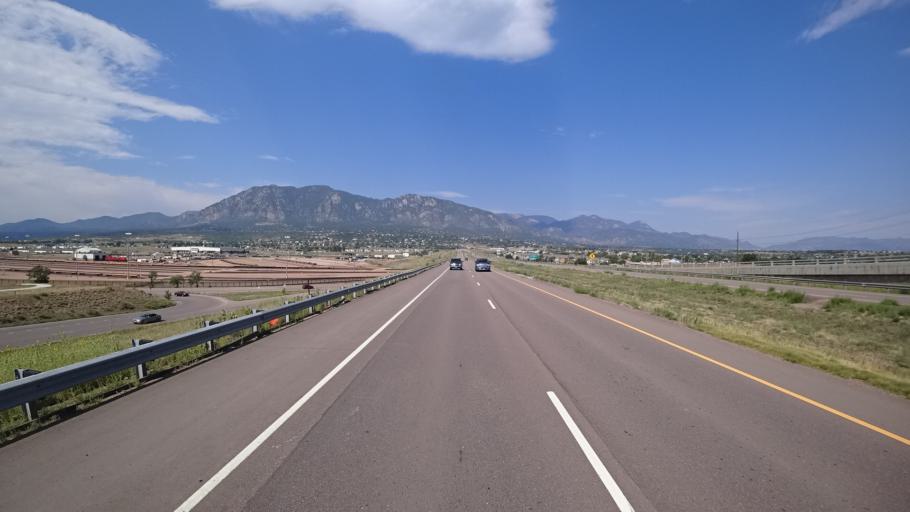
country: US
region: Colorado
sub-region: El Paso County
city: Stratmoor
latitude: 38.7656
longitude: -104.7948
